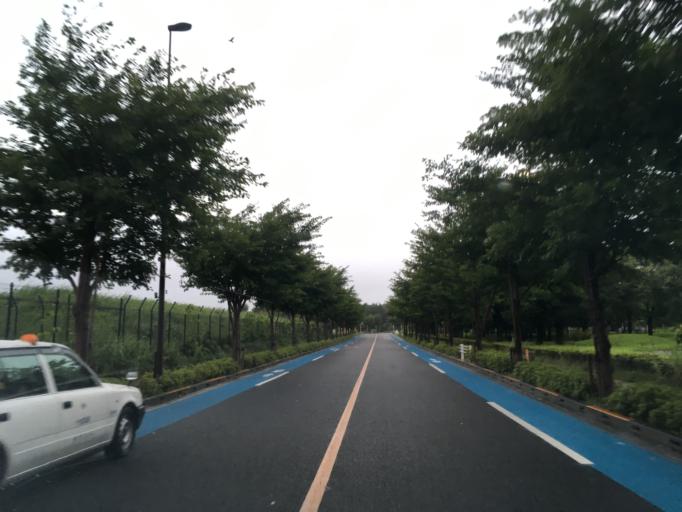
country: JP
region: Tokyo
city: Chofugaoka
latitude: 35.6764
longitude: 139.5282
